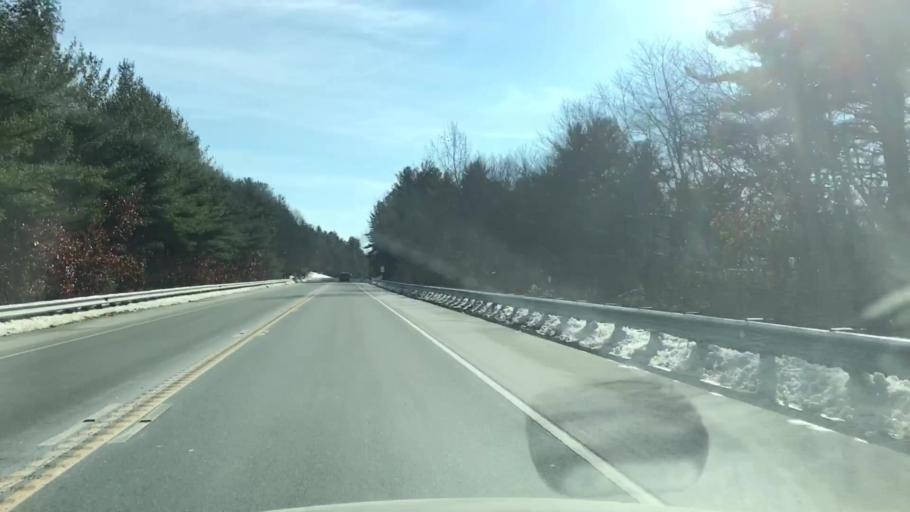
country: US
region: New Hampshire
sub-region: Hillsborough County
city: Milford
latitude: 42.8595
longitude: -71.6121
